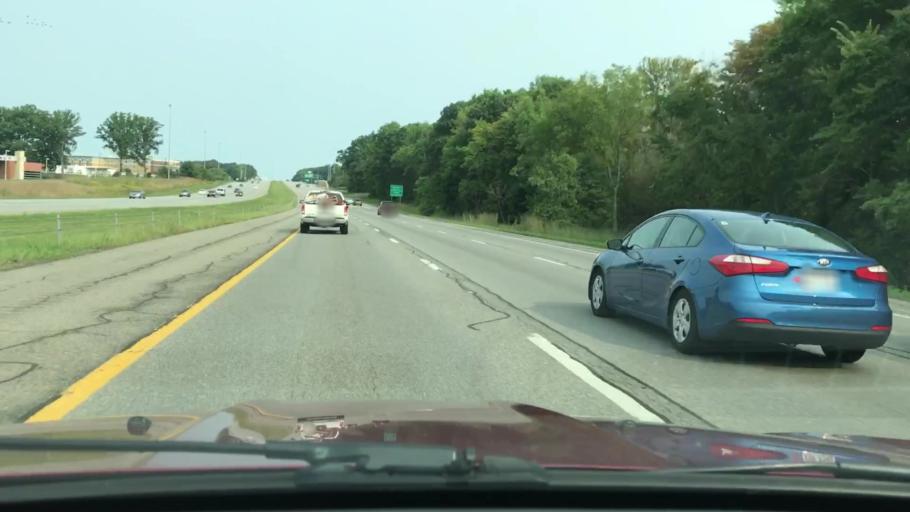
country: US
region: Ohio
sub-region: Summit County
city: Greensburg
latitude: 40.9572
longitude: -81.4574
